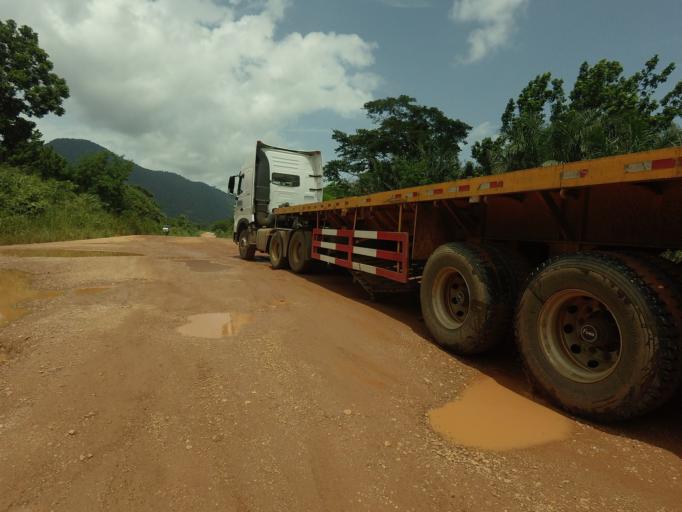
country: GH
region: Volta
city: Ho
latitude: 6.7767
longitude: 0.3645
